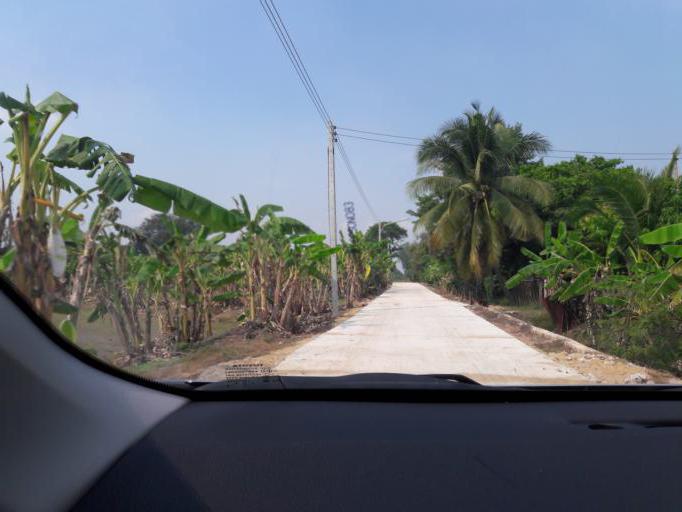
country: TH
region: Ang Thong
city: Ang Thong
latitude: 14.5601
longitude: 100.4247
